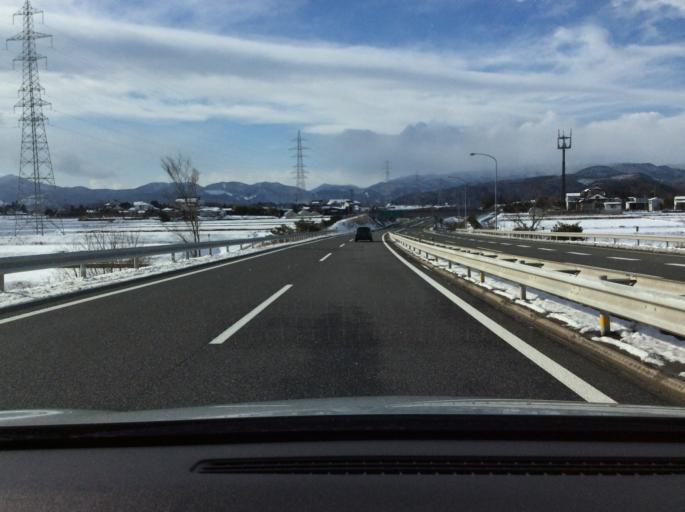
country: JP
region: Fukushima
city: Motomiya
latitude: 37.4634
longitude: 140.3587
